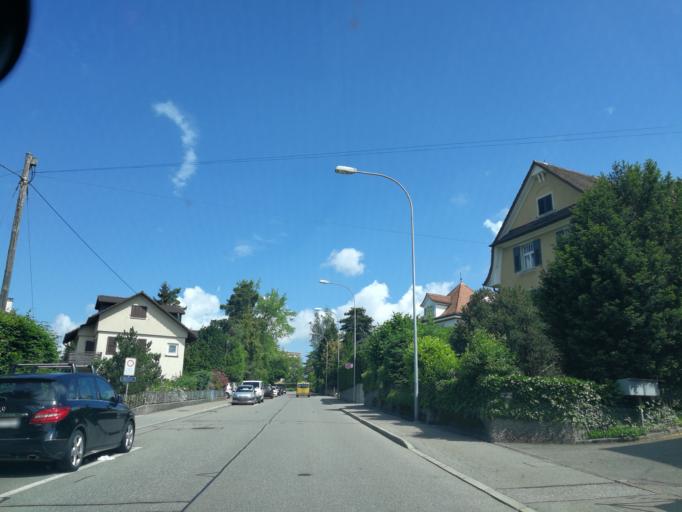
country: CH
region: Zurich
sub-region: Bezirk Meilen
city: Erlenbach
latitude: 47.3057
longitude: 8.5936
